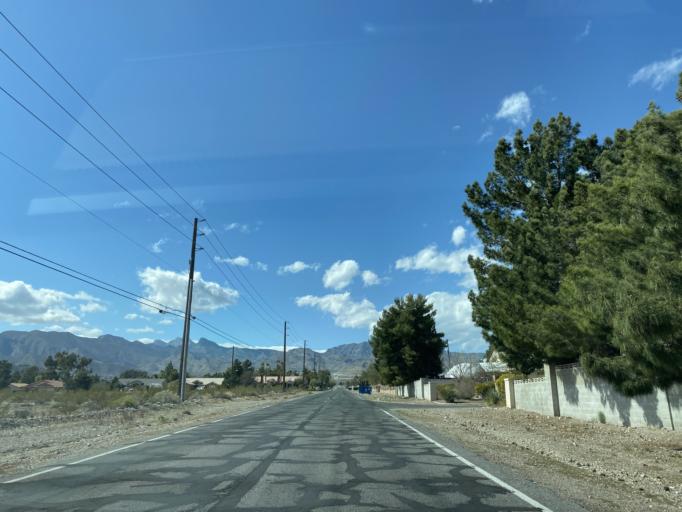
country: US
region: Nevada
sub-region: Clark County
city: Summerlin South
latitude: 36.2556
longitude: -115.2907
